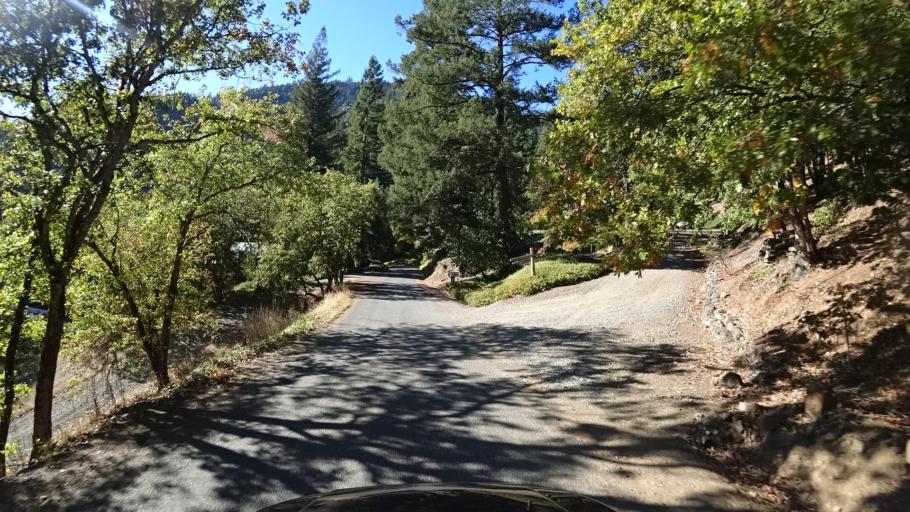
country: US
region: California
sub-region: Humboldt County
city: Willow Creek
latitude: 41.2729
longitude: -123.3005
